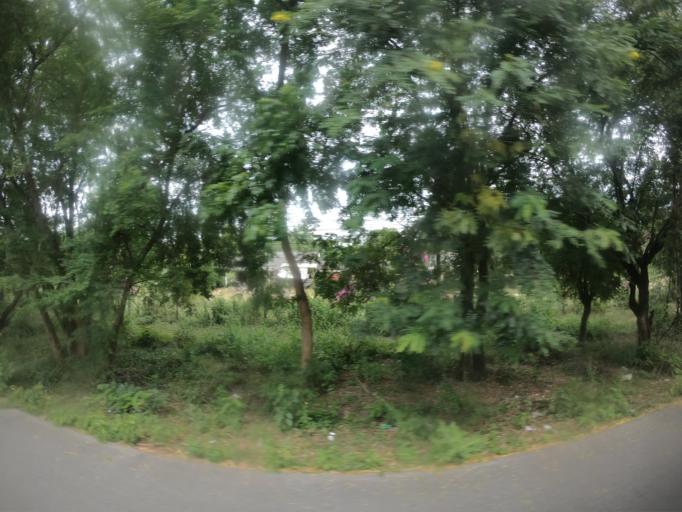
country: TH
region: Maha Sarakham
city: Maha Sarakham
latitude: 16.1480
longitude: 103.4024
